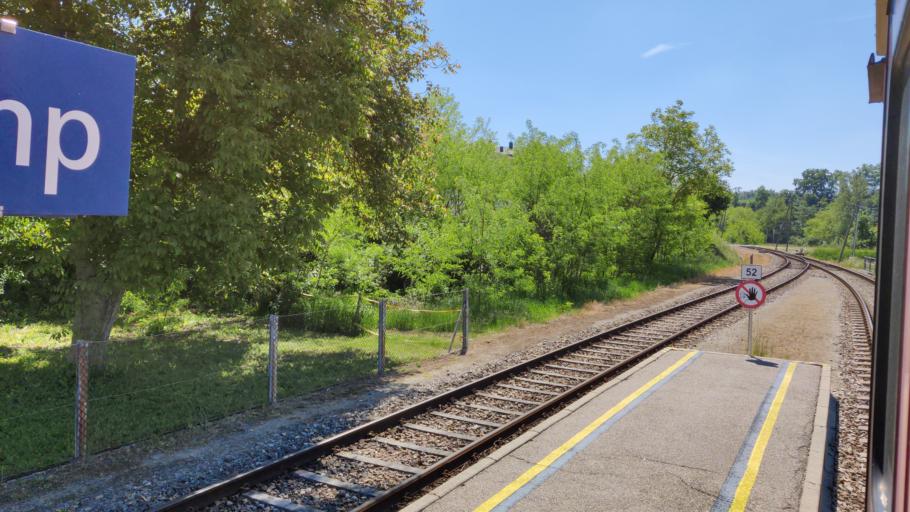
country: AT
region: Lower Austria
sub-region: Politischer Bezirk Horn
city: Gars am Kamp
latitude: 48.5575
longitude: 15.6735
